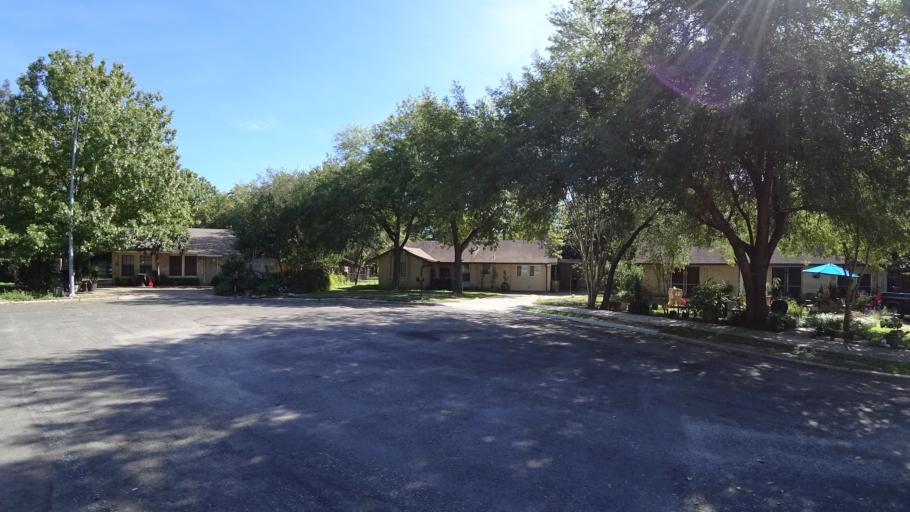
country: US
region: Texas
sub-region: Travis County
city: Onion Creek
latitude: 30.1969
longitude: -97.7523
